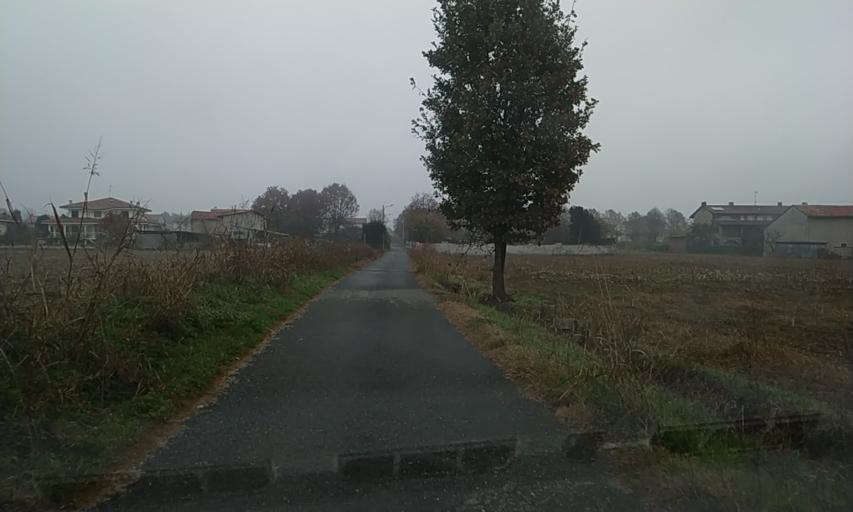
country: IT
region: Piedmont
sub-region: Provincia di Vercelli
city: Alice Castello
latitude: 45.3678
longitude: 8.0669
